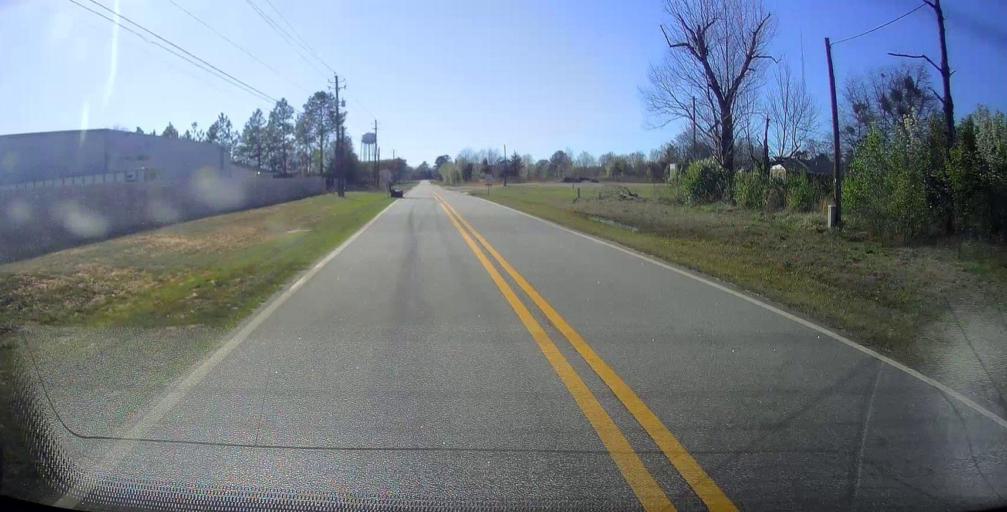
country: US
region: Georgia
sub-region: Peach County
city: Byron
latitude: 32.6516
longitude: -83.7478
